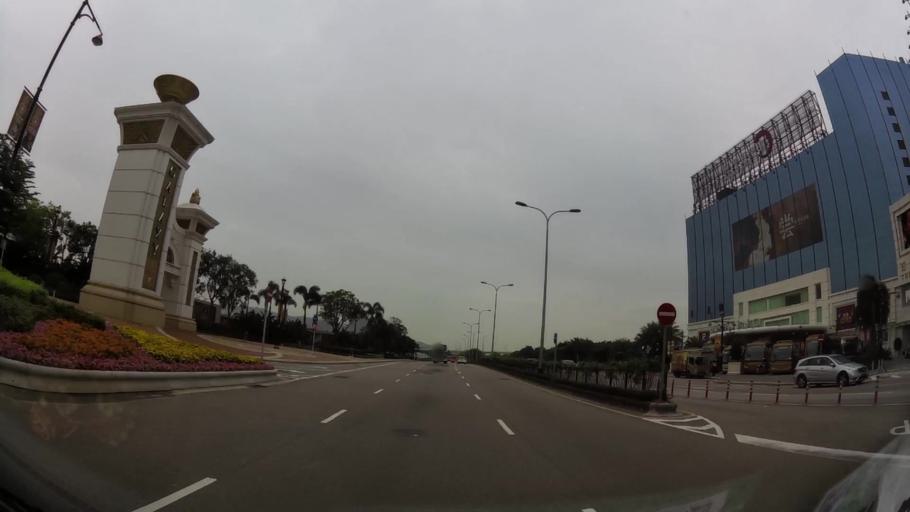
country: MO
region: Macau
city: Macau
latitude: 22.1461
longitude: 113.5528
